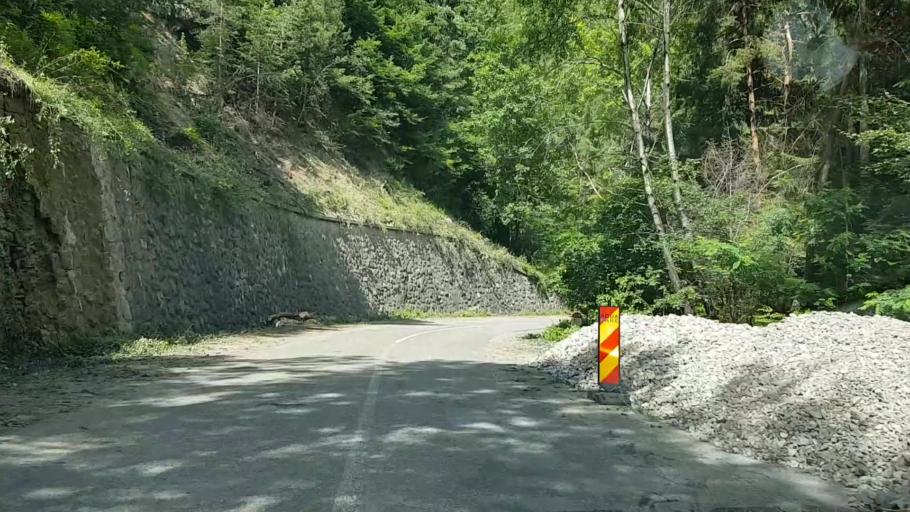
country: RO
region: Neamt
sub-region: Comuna Ceahlau
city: Ceahlau
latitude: 47.0532
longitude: 25.9805
